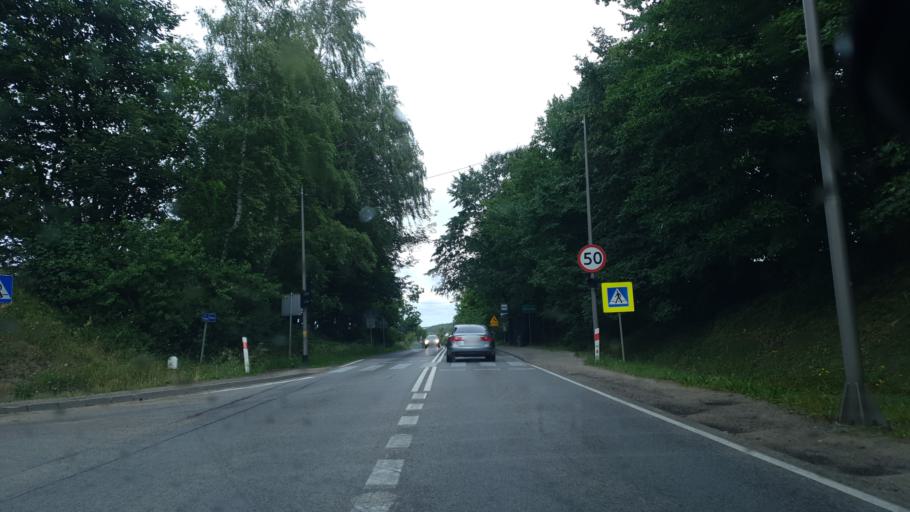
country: PL
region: Pomeranian Voivodeship
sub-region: Powiat kartuski
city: Chwaszczyno
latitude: 54.4518
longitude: 18.4396
